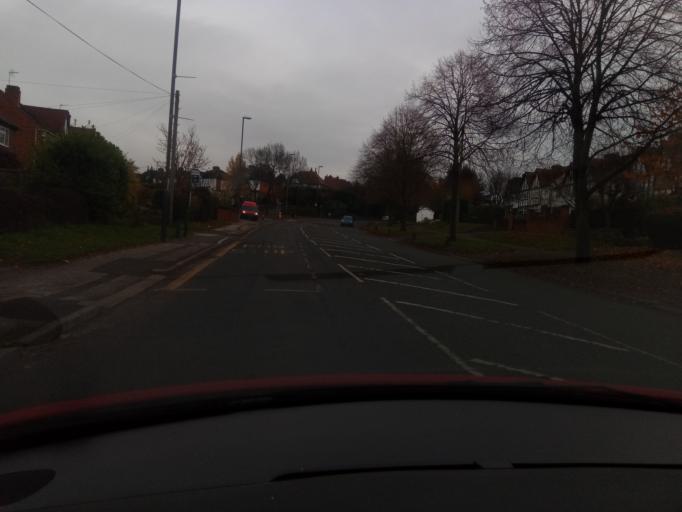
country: GB
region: England
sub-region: Derby
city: Derby
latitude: 52.9230
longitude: -1.4351
